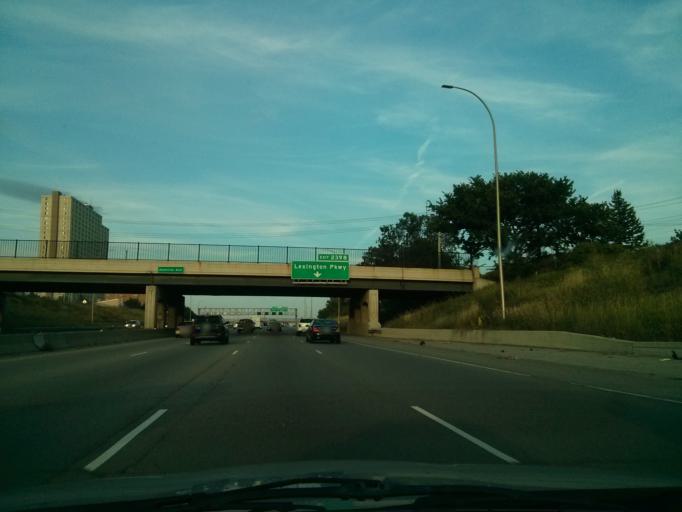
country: US
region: Minnesota
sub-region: Ramsey County
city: Falcon Heights
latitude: 44.9517
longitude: -93.1576
